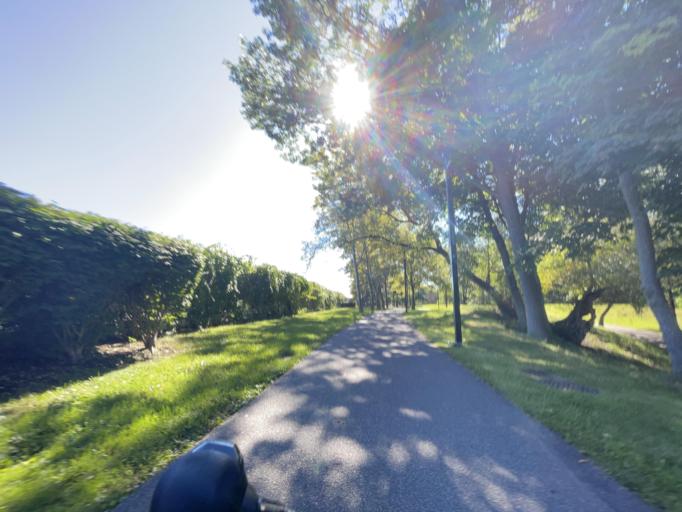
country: US
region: Massachusetts
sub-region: Suffolk County
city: Jamaica Plain
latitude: 42.3049
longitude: -71.1114
